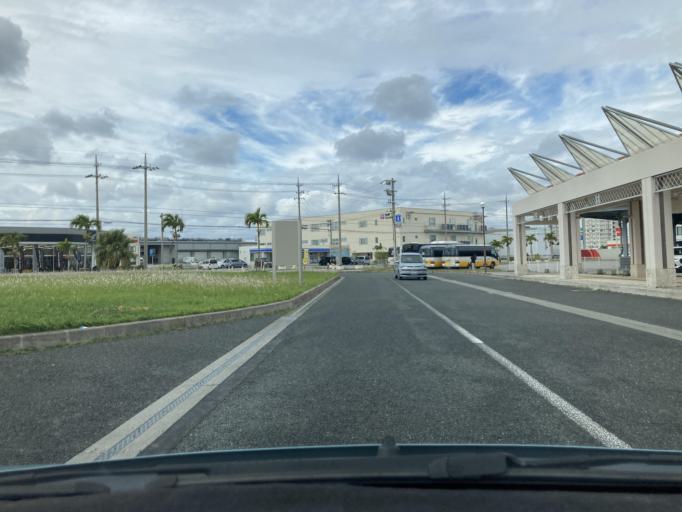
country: JP
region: Okinawa
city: Itoman
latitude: 26.1576
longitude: 127.6552
